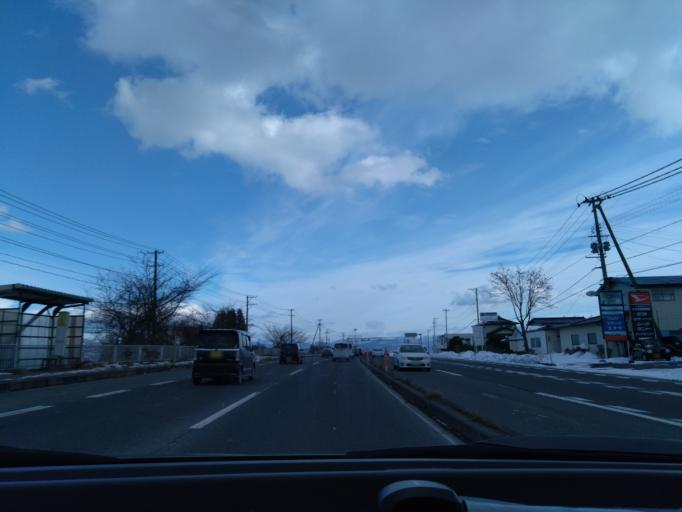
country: JP
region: Iwate
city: Shizukuishi
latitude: 39.7018
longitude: 141.0479
